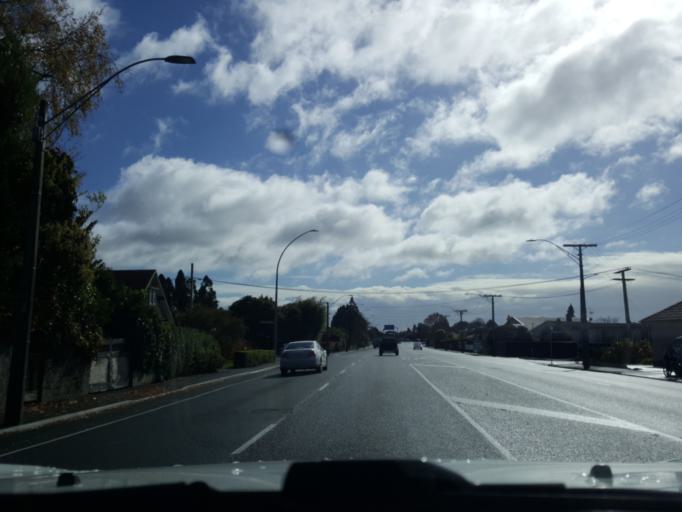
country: NZ
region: Waikato
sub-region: Hamilton City
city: Hamilton
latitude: -37.7729
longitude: 175.2638
